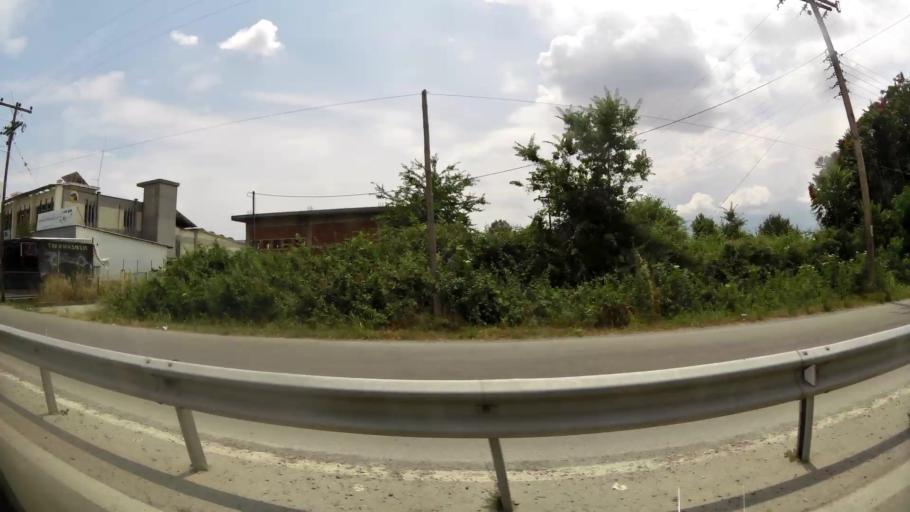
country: GR
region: Central Macedonia
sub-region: Nomos Pierias
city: Peristasi
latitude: 40.2733
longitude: 22.5495
